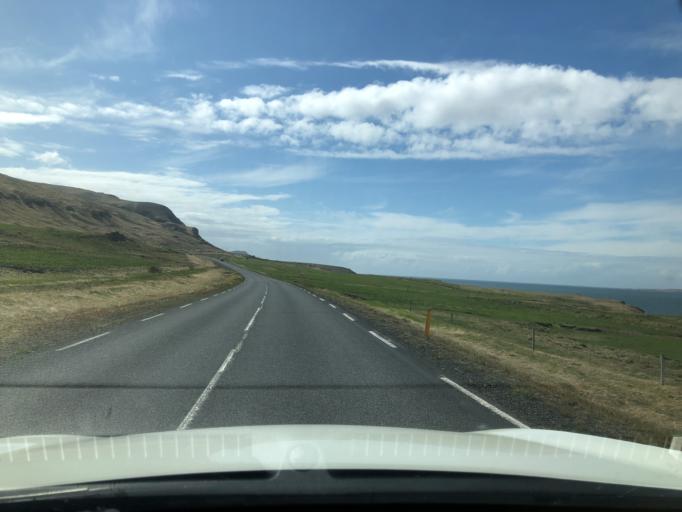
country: IS
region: Capital Region
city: Mosfellsbaer
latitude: 64.3299
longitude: -21.7418
